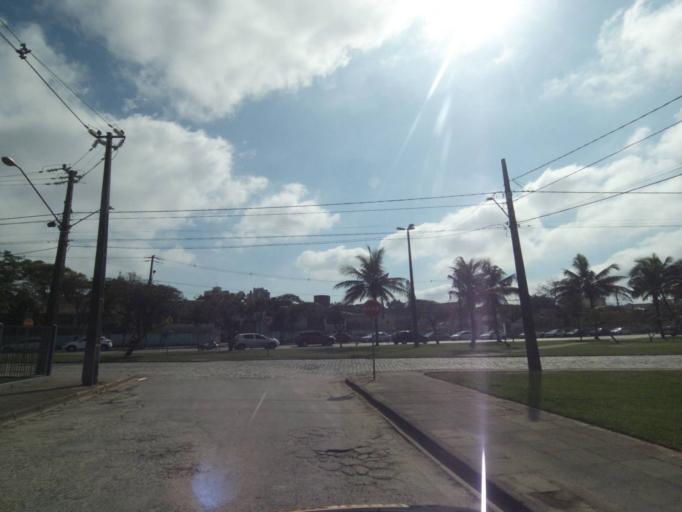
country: BR
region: Parana
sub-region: Paranagua
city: Paranagua
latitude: -25.5241
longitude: -48.5093
